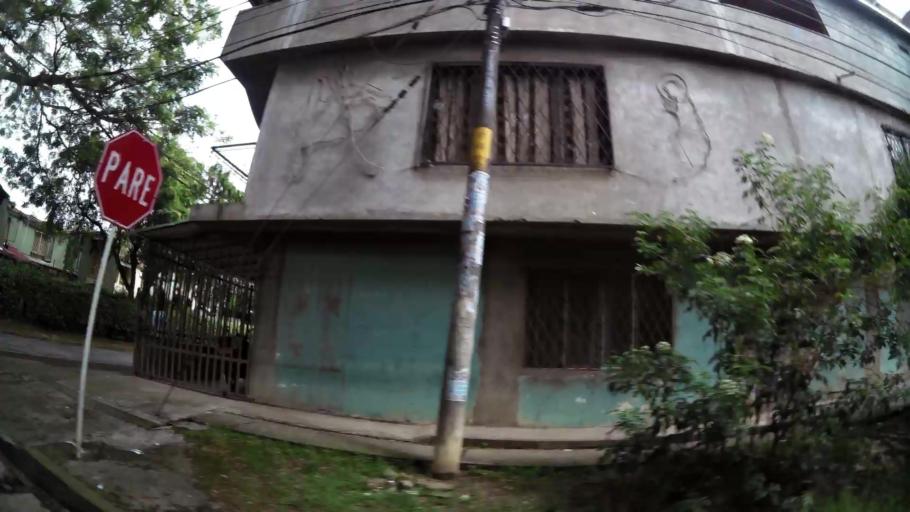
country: CO
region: Valle del Cauca
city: Cali
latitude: 3.3922
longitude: -76.5502
